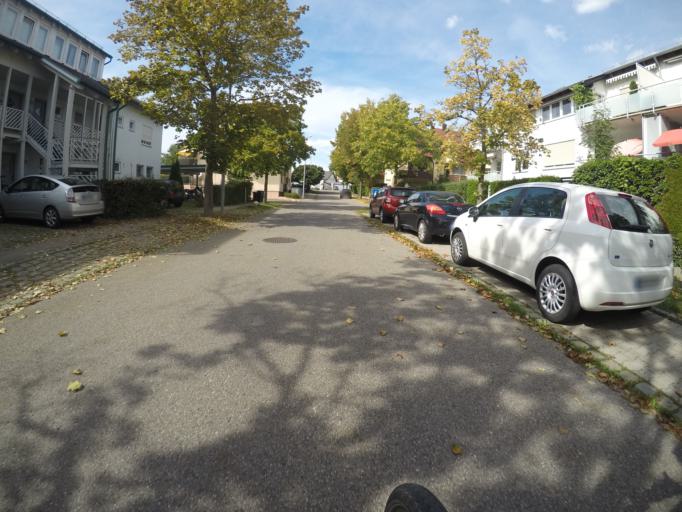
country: DE
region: Baden-Wuerttemberg
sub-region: Regierungsbezirk Stuttgart
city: Gartringen
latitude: 48.6464
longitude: 8.8972
